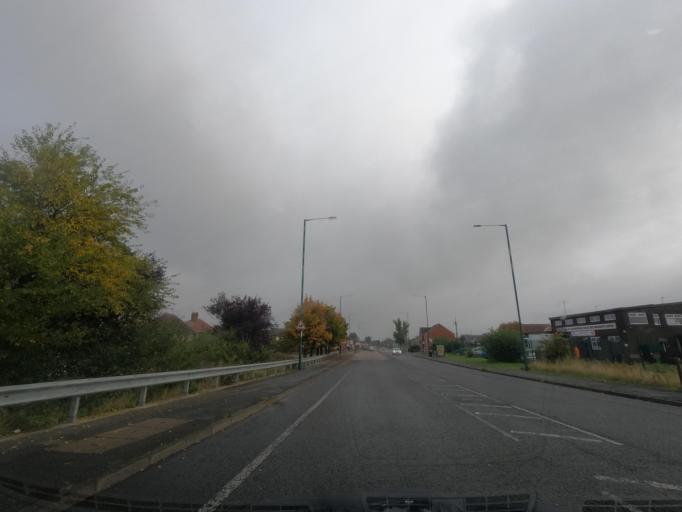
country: GB
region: England
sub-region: Redcar and Cleveland
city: South Bank
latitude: 54.5752
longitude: -1.1517
